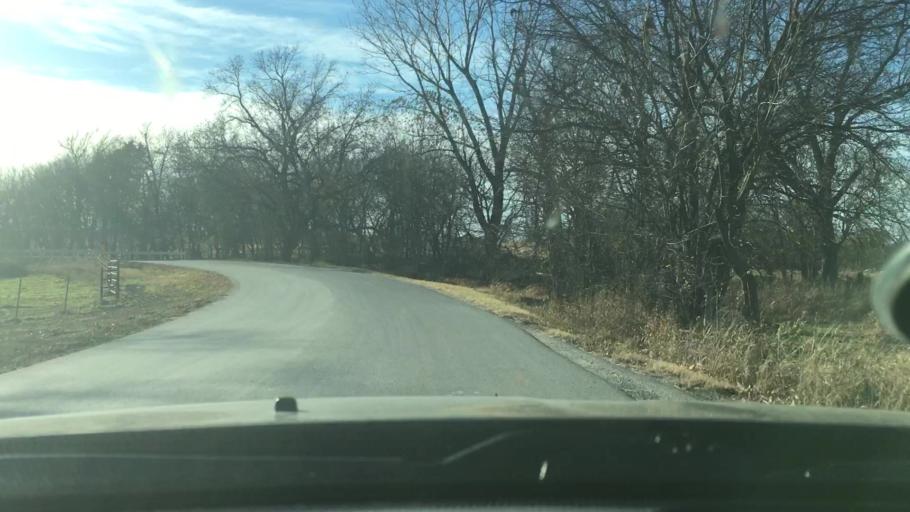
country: US
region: Oklahoma
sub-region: Murray County
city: Davis
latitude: 34.4994
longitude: -97.1573
